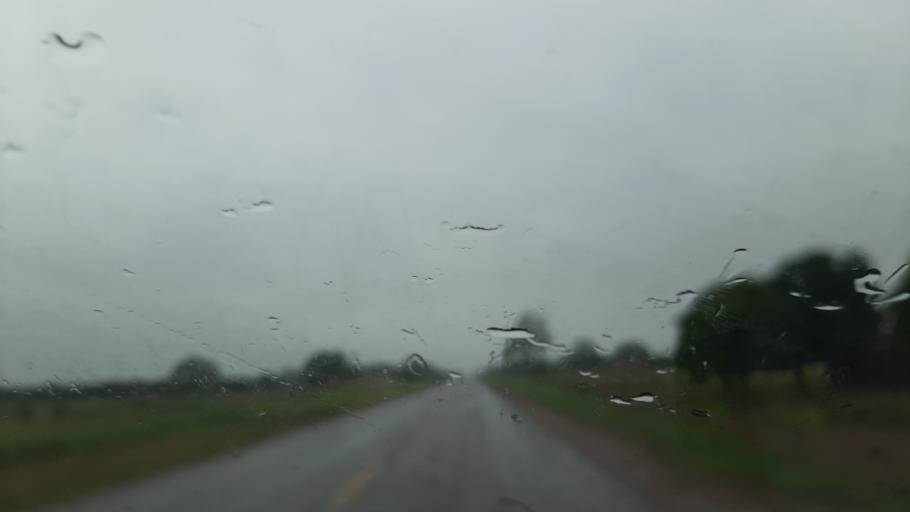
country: BO
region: Santa Cruz
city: Okinawa Numero Uno
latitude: -16.8580
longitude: -62.6103
